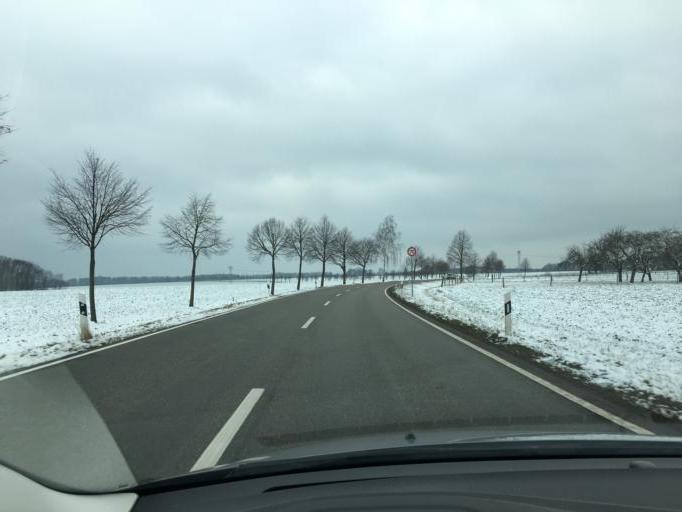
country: DE
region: Saxony
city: Bad Lausick
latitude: 51.1366
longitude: 12.6865
